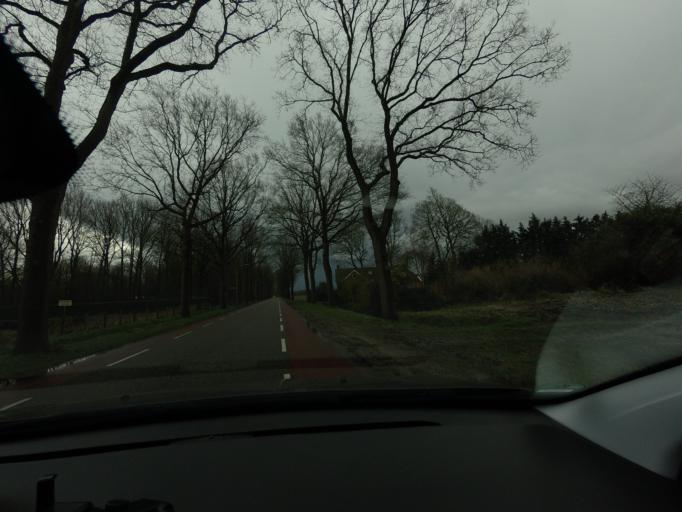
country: NL
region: Drenthe
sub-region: Gemeente Borger-Odoorn
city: Borger
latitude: 52.9819
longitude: 6.7852
